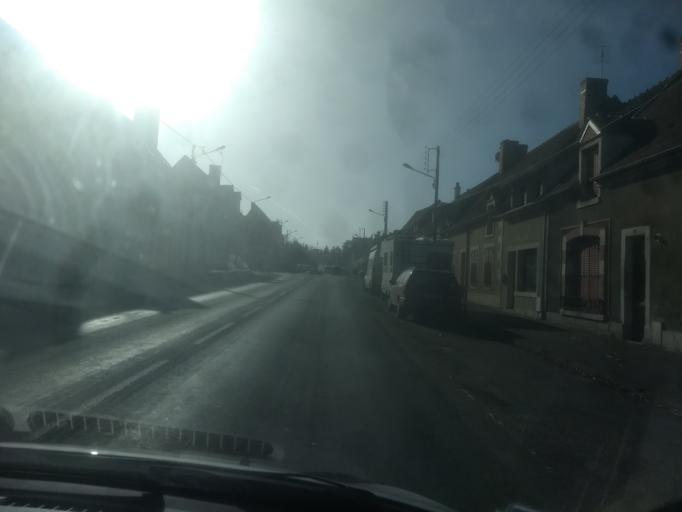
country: FR
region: Centre
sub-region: Departement du Cher
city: Orval
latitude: 46.7702
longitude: 2.4329
